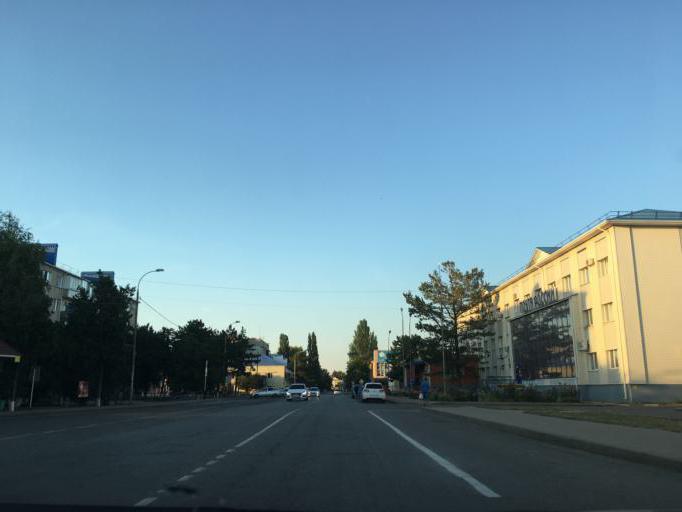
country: RU
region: Krasnodarskiy
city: Kushchevskaya
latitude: 46.5659
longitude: 39.6292
